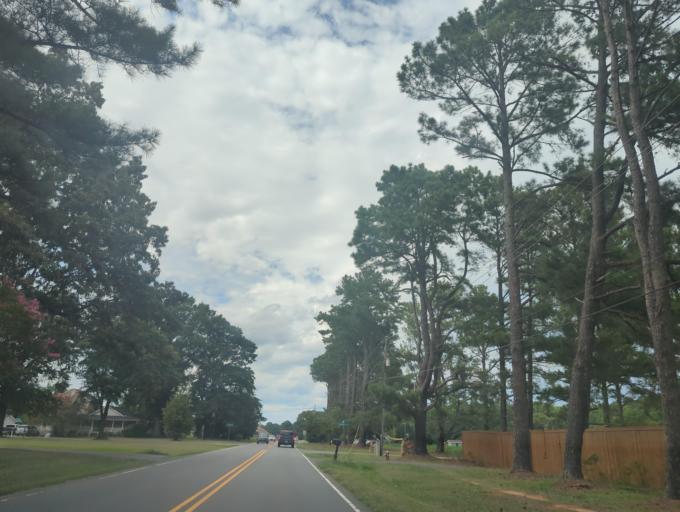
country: US
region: North Carolina
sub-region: Wake County
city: Fuquay-Varina
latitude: 35.6173
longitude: -78.7749
